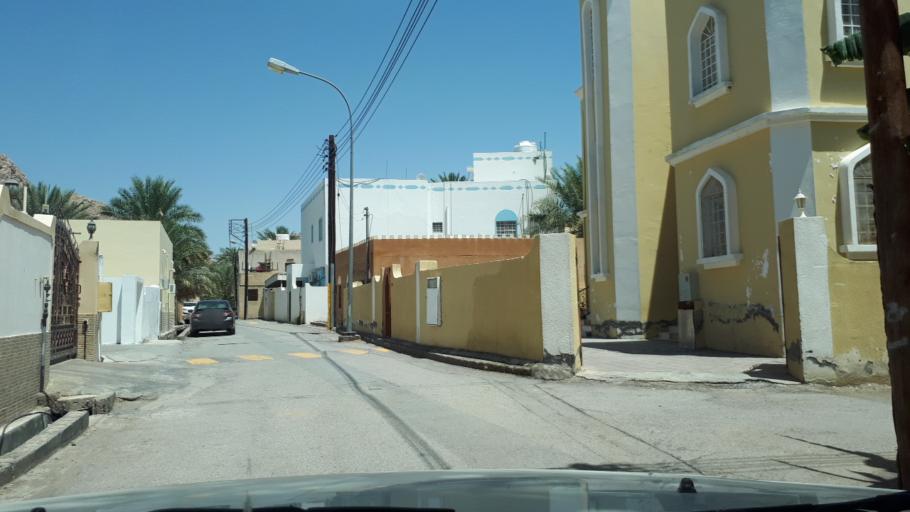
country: OM
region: Muhafazat ad Dakhiliyah
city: Nizwa
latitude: 22.8825
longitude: 57.5270
